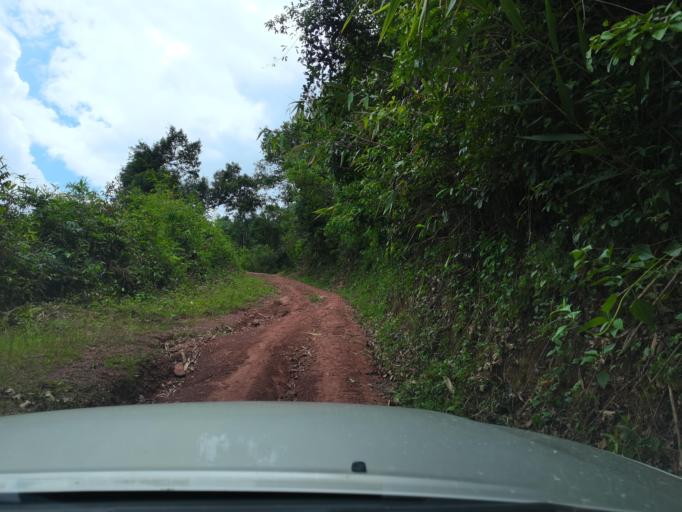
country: LA
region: Loungnamtha
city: Muang Nale
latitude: 20.5053
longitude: 101.0862
